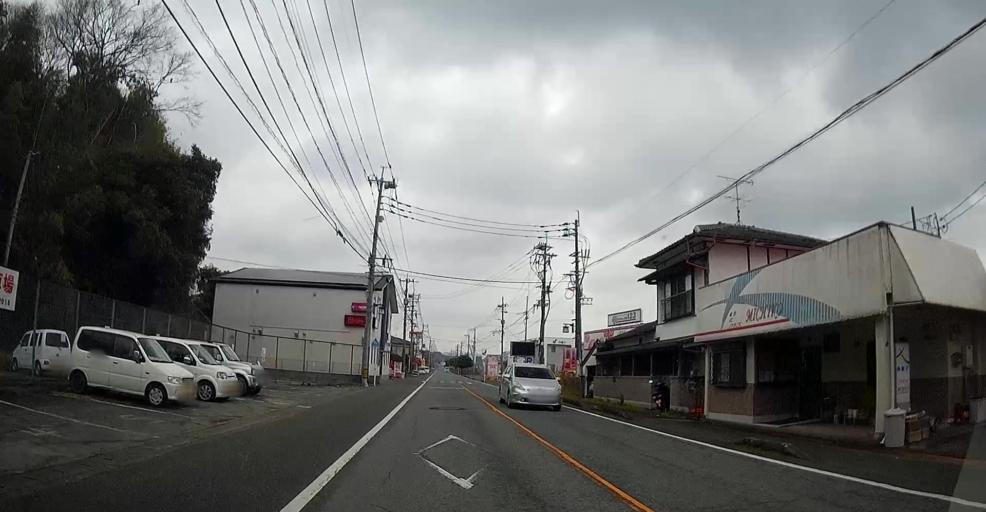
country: JP
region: Kumamoto
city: Matsubase
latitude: 32.6511
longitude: 130.6900
